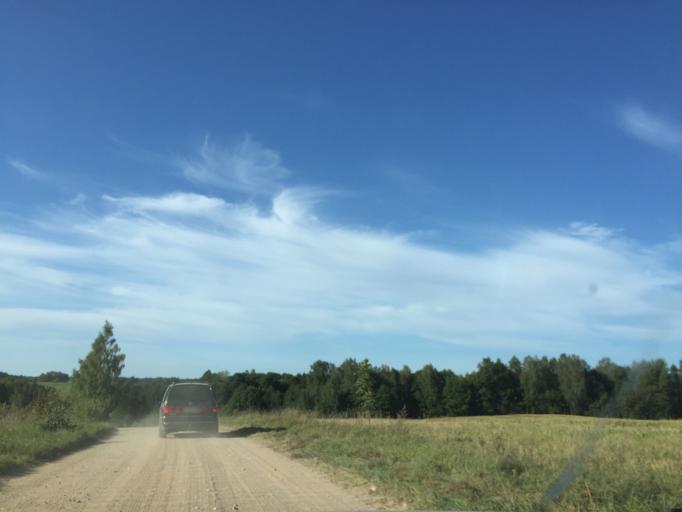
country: LT
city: Zarasai
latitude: 55.7924
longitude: 25.9539
